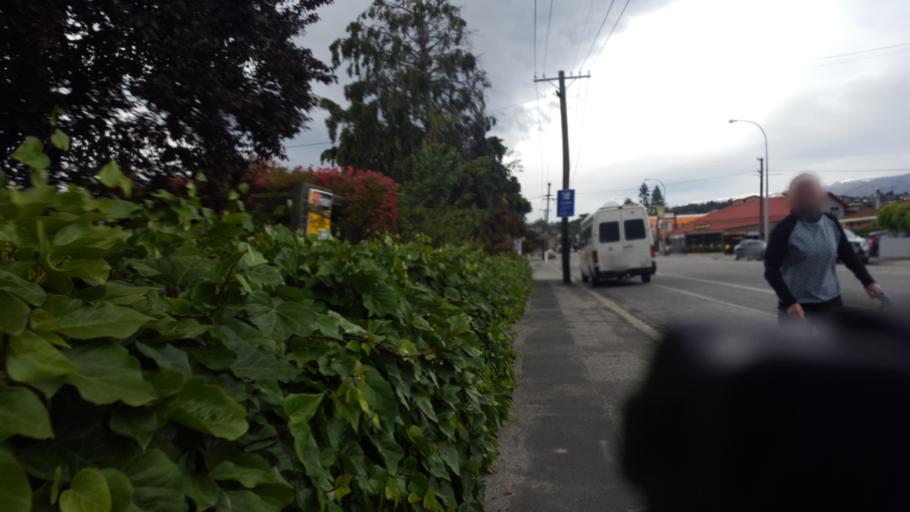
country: NZ
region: Otago
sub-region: Queenstown-Lakes District
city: Wanaka
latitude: -45.2518
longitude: 169.3957
